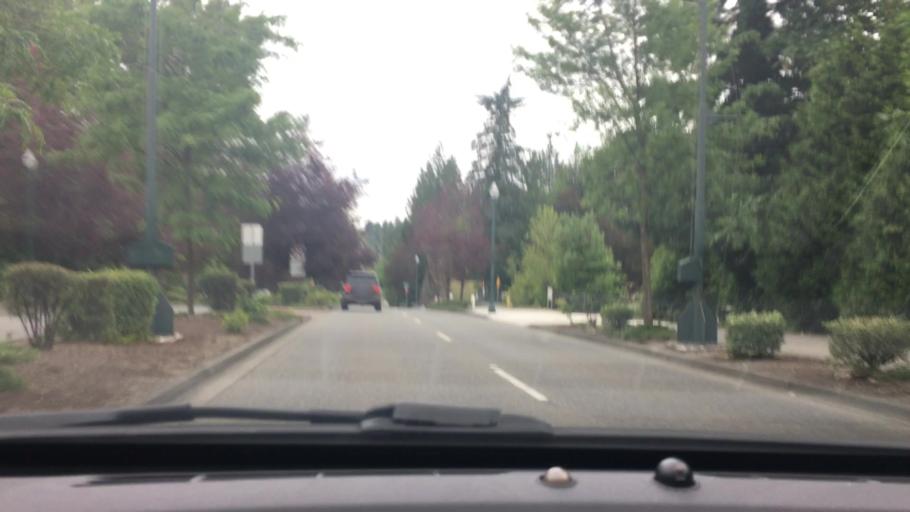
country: US
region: Washington
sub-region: King County
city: City of Sammamish
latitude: 47.6074
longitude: -122.0354
